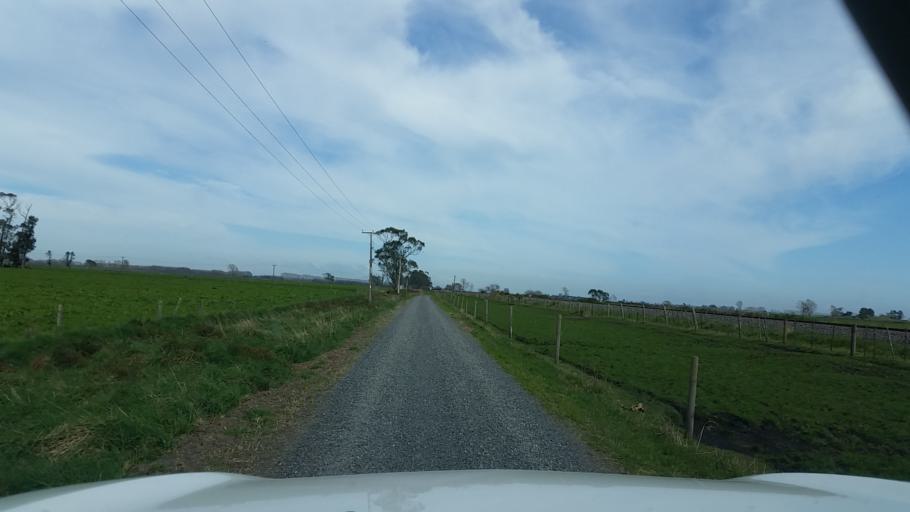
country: NZ
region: Waikato
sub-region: Waipa District
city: Cambridge
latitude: -37.6833
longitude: 175.4543
